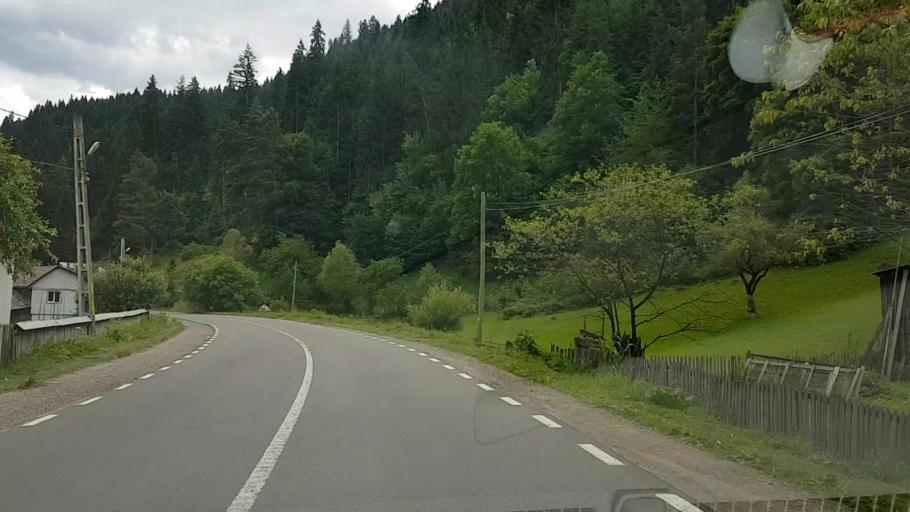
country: RO
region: Neamt
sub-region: Comuna Poiana Teiului
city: Poiana Teiului
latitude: 47.1083
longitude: 25.9316
